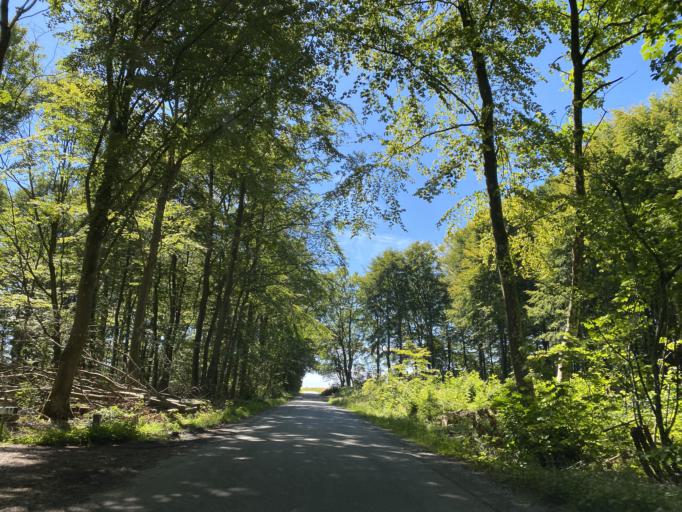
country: DK
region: South Denmark
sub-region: Vejle Kommune
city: Vejle
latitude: 55.6372
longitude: 9.5423
